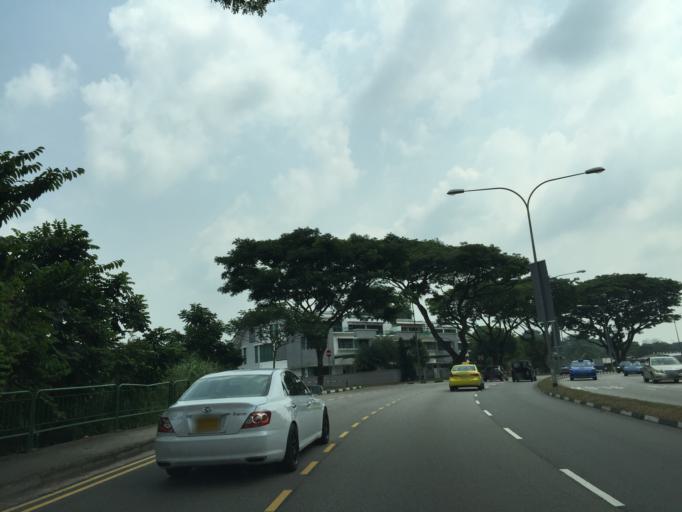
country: SG
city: Singapore
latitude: 1.3342
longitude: 103.8374
